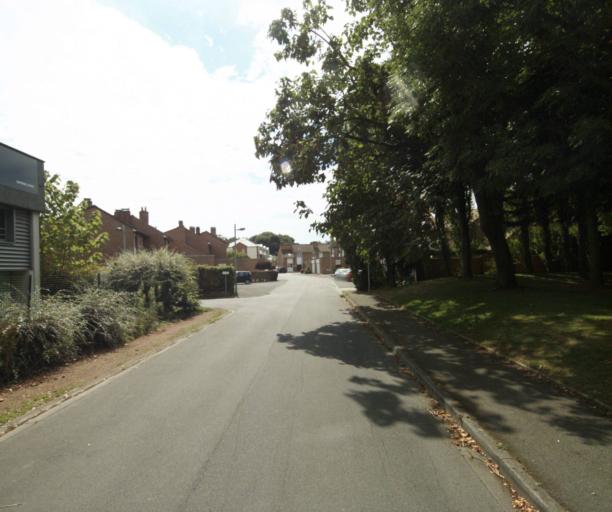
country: FR
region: Nord-Pas-de-Calais
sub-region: Departement du Nord
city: Mons-en-Baroeul
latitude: 50.6497
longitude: 3.1078
